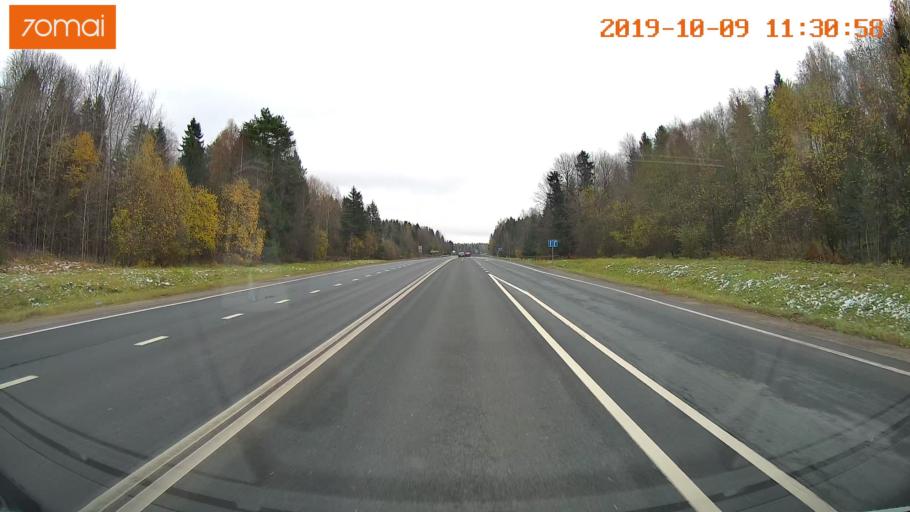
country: RU
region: Vologda
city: Gryazovets
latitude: 59.0494
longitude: 40.0866
